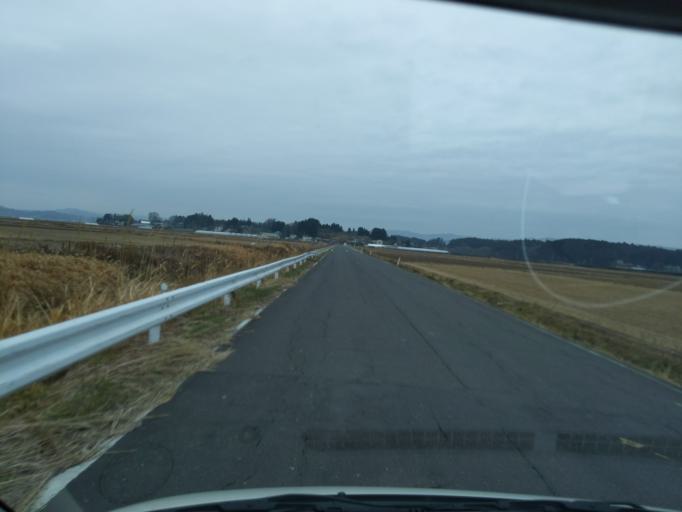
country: JP
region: Miyagi
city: Wakuya
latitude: 38.7298
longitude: 141.2455
